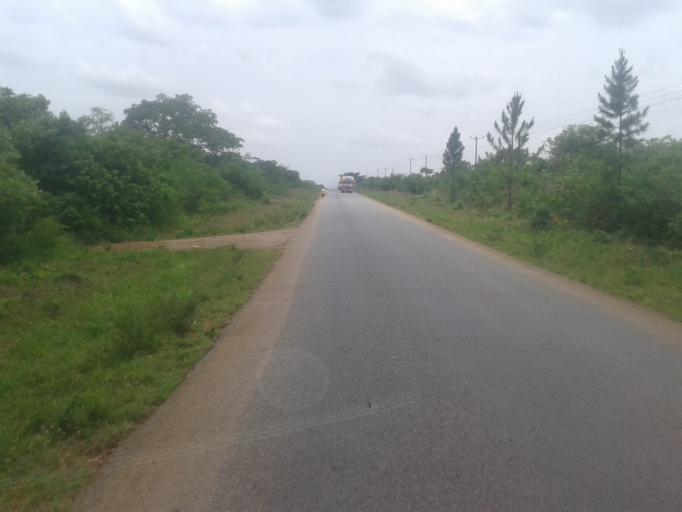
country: UG
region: Western Region
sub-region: Kiryandongo District
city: Masindi Port
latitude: 1.4822
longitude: 32.1391
